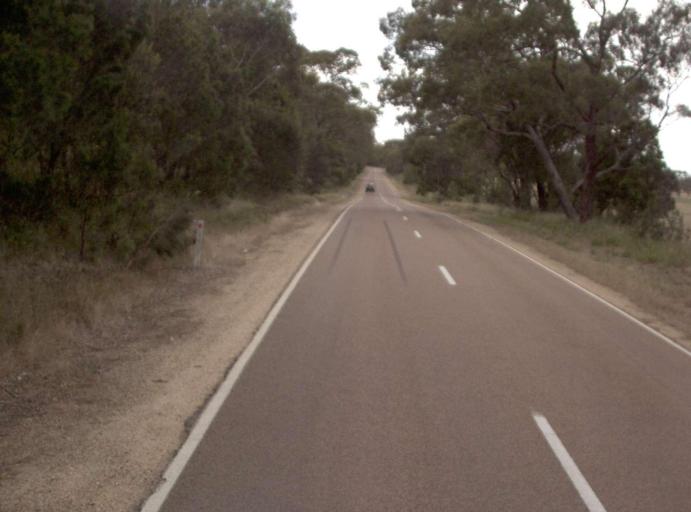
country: AU
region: Victoria
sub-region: Wellington
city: Sale
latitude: -38.0016
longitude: 147.3060
